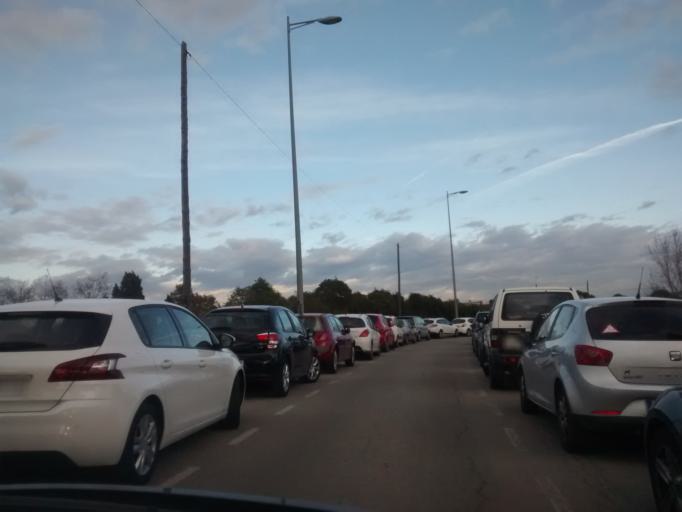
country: ES
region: Catalonia
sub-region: Provincia de Barcelona
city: Rubi
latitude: 41.4760
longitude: 2.0472
